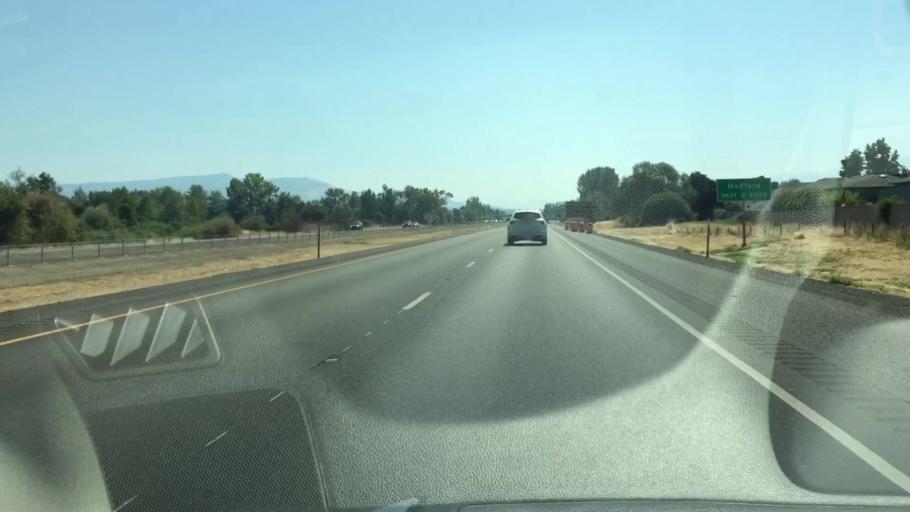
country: US
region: Oregon
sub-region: Jackson County
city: Central Point
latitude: 42.3701
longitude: -122.8942
